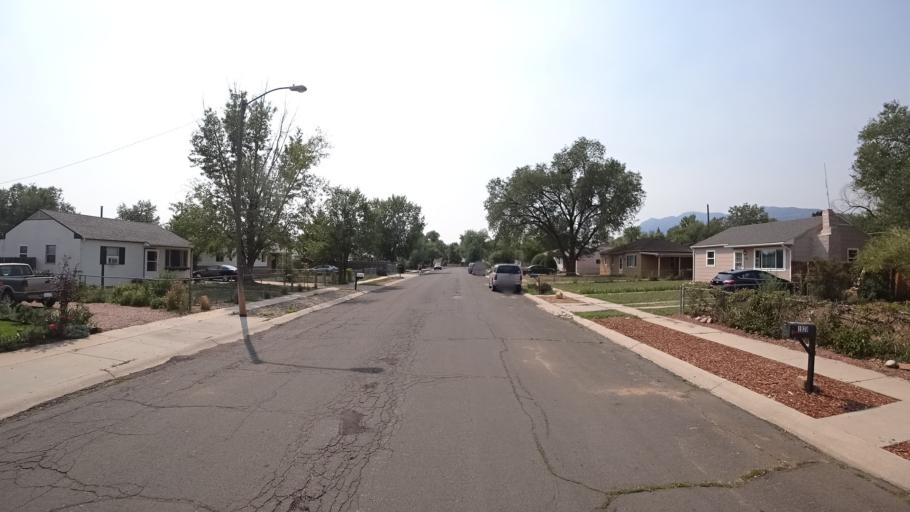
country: US
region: Colorado
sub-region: El Paso County
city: Colorado Springs
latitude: 38.8051
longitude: -104.8094
